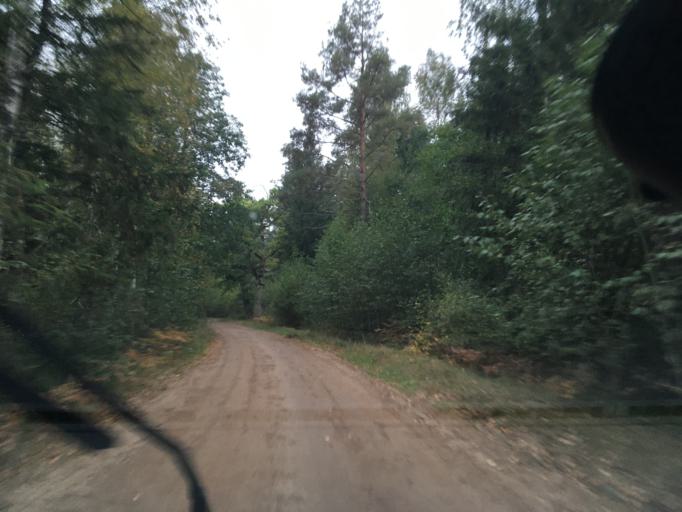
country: LV
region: Kuldigas Rajons
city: Kuldiga
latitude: 57.0229
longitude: 21.9964
